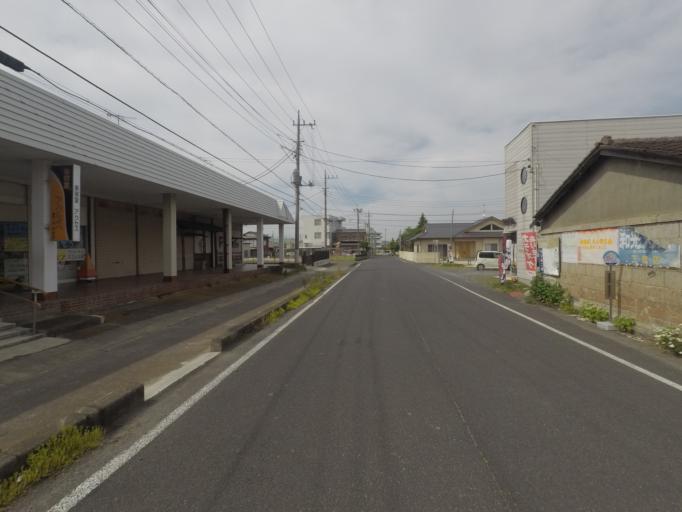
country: JP
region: Ibaraki
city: Makabe
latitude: 36.2769
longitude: 140.0949
